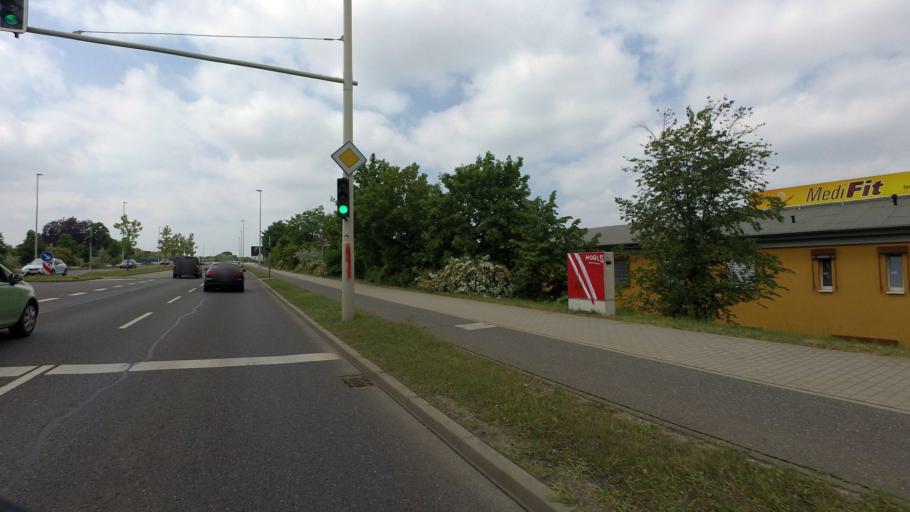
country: DE
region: Brandenburg
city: Cottbus
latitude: 51.7500
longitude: 14.3428
